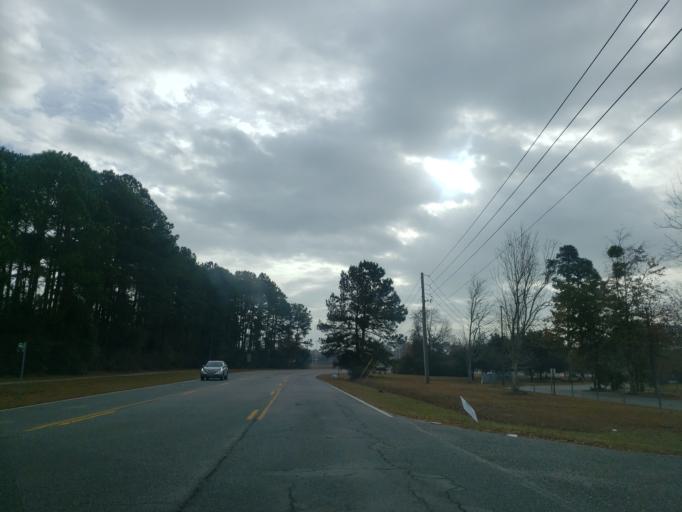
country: US
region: Georgia
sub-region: Chatham County
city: Whitemarsh Island
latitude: 32.0402
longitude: -81.0094
